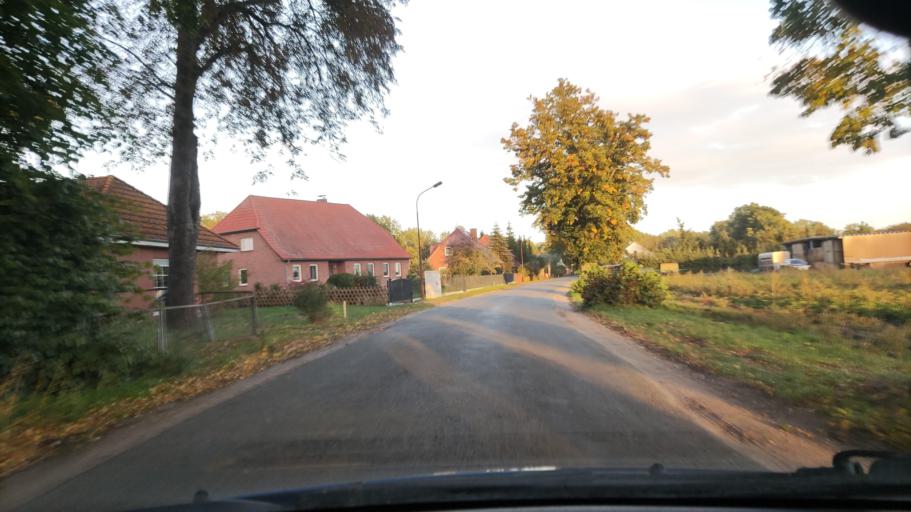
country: DE
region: Mecklenburg-Vorpommern
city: Lubtheen
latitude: 53.3236
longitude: 11.0557
